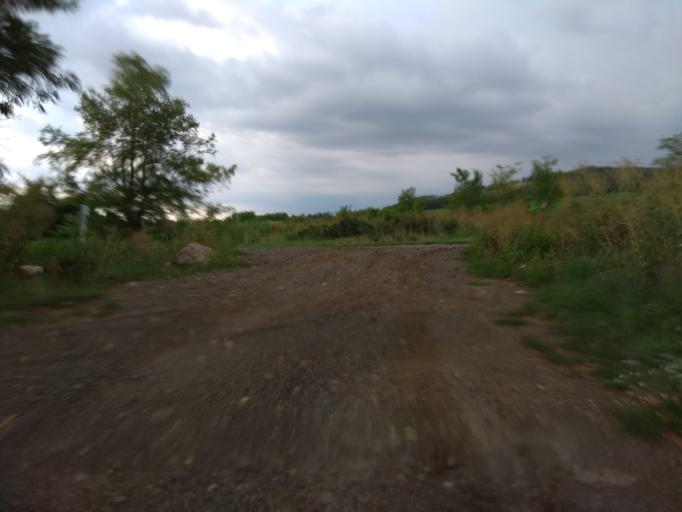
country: HU
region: Borsod-Abauj-Zemplen
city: Monok
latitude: 48.1726
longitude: 21.1199
